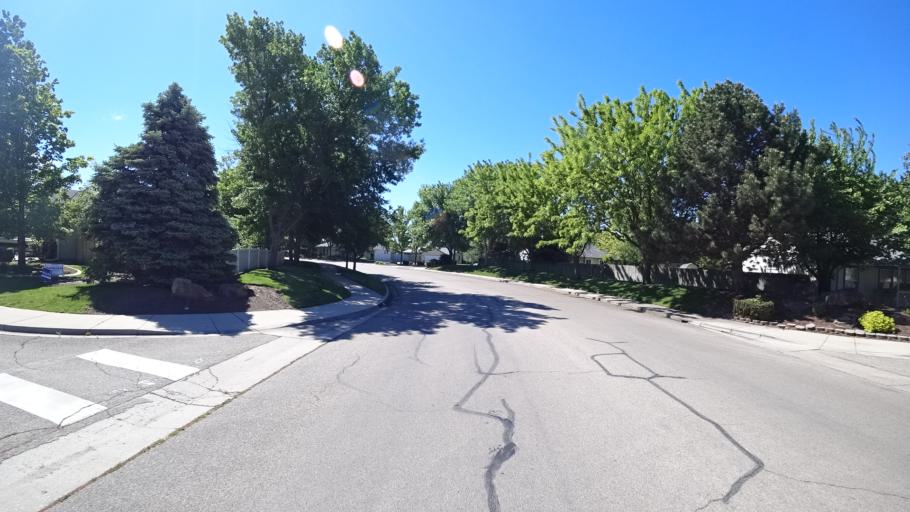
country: US
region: Idaho
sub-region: Ada County
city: Meridian
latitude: 43.6219
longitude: -116.3647
